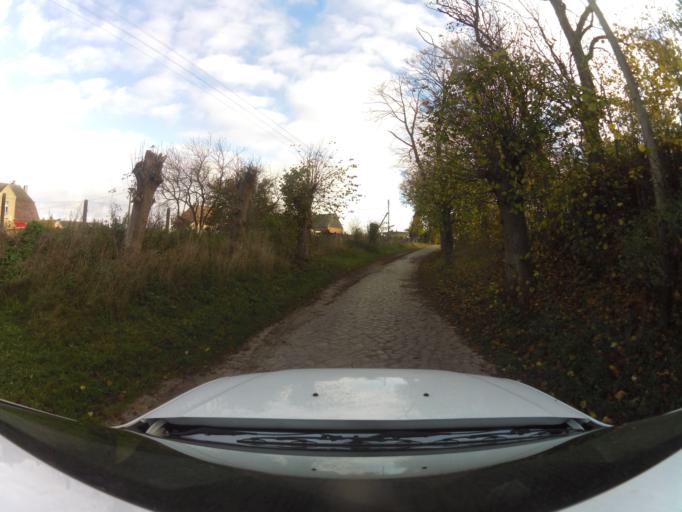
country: PL
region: West Pomeranian Voivodeship
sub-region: Powiat gryficki
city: Cerkwica
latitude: 54.0613
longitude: 15.1694
